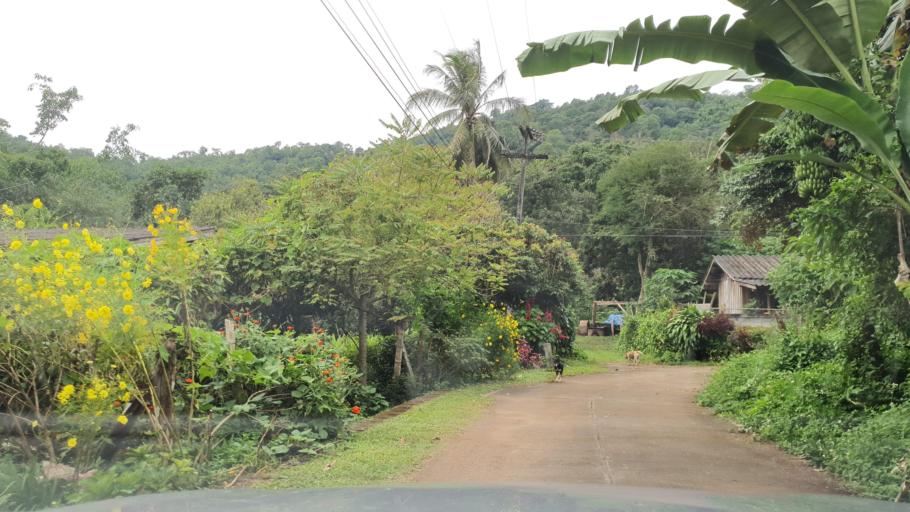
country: TH
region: Chiang Mai
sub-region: Amphoe Chiang Dao
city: Chiang Dao
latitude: 19.2496
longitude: 98.9230
